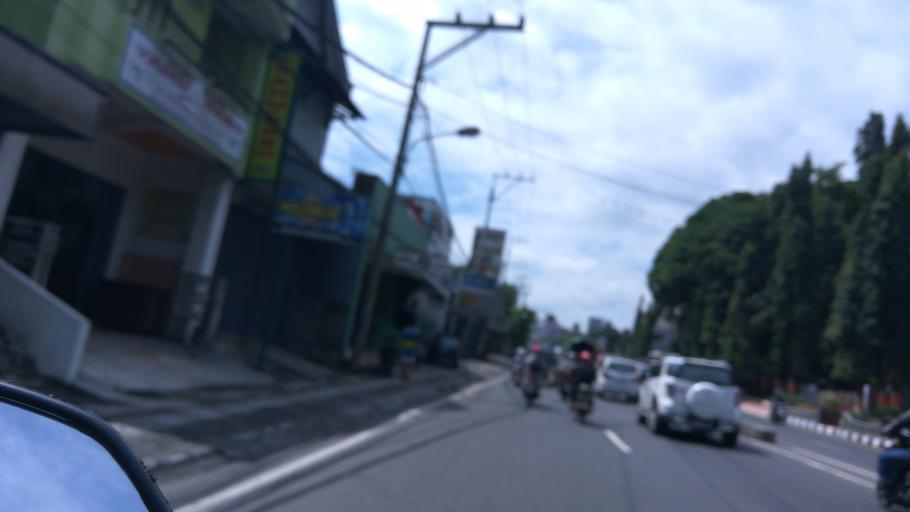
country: ID
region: Central Java
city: Ungaran
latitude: -7.1304
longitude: 110.4041
